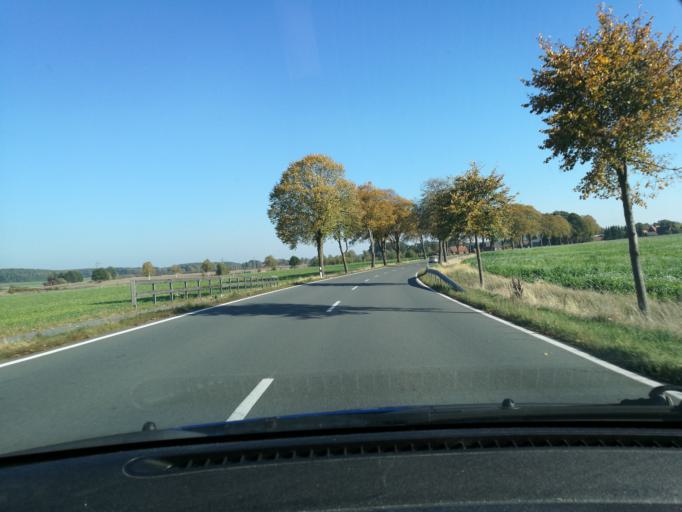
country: DE
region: Lower Saxony
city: Nahrendorf
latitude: 53.1613
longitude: 10.8032
